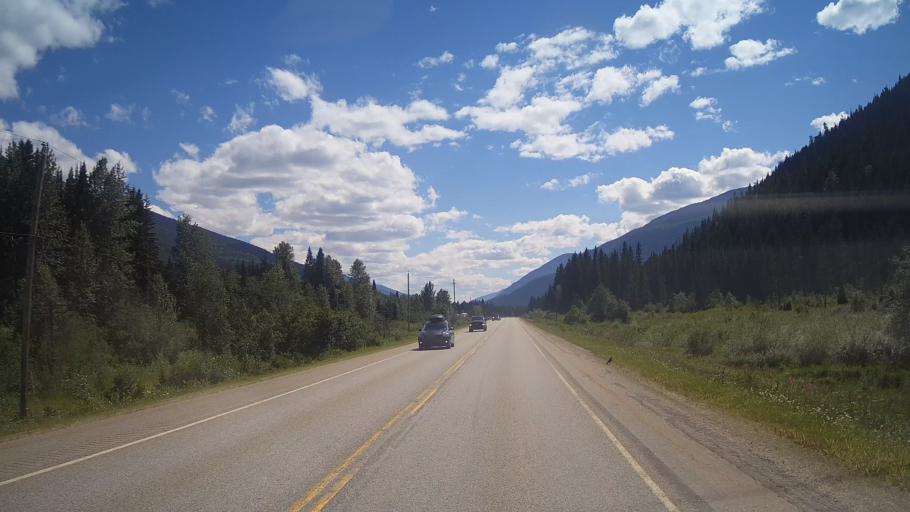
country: CA
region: Alberta
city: Jasper Park Lodge
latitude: 52.5808
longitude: -119.0958
